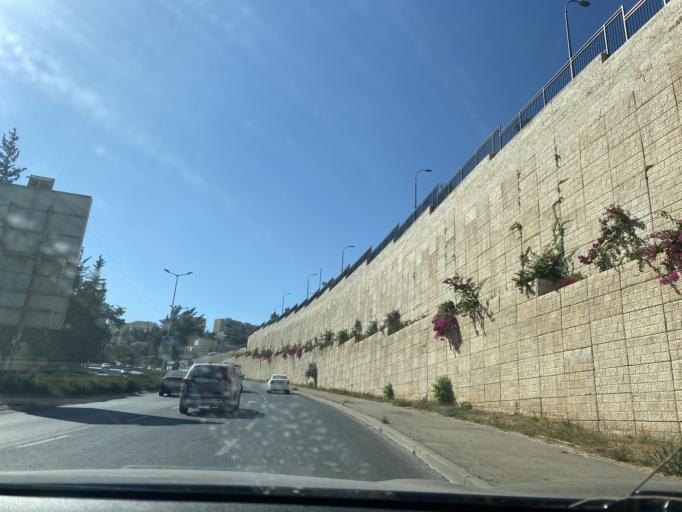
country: PS
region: West Bank
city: Bayt Iksa
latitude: 31.8111
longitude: 35.2034
